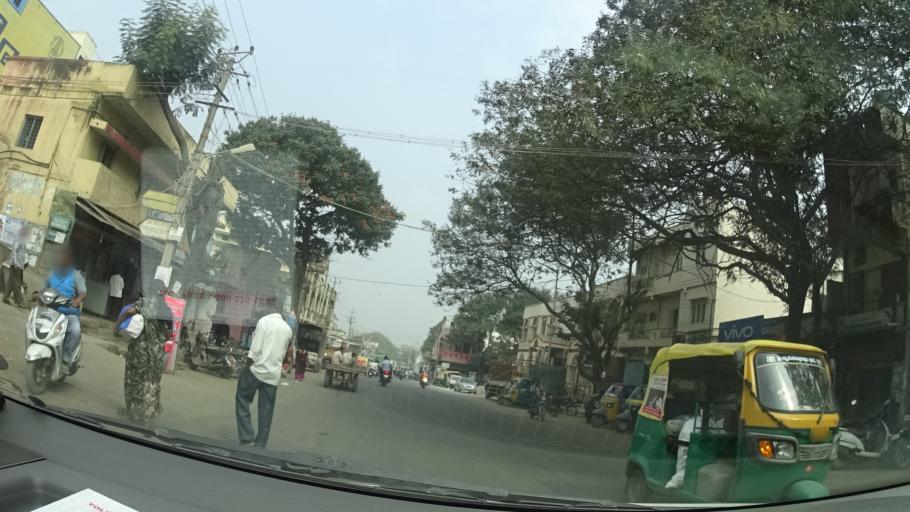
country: IN
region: Karnataka
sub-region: Bangalore Urban
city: Bangalore
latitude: 13.0223
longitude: 77.6194
